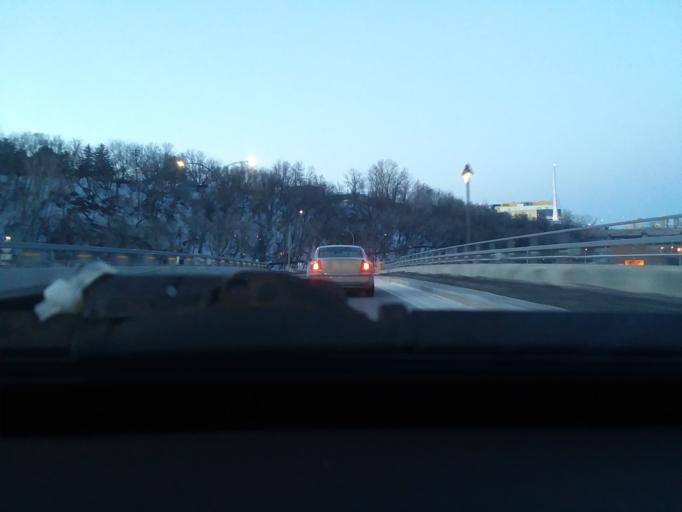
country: CA
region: Quebec
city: Saint-Raymond
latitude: 45.4658
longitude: -73.6064
